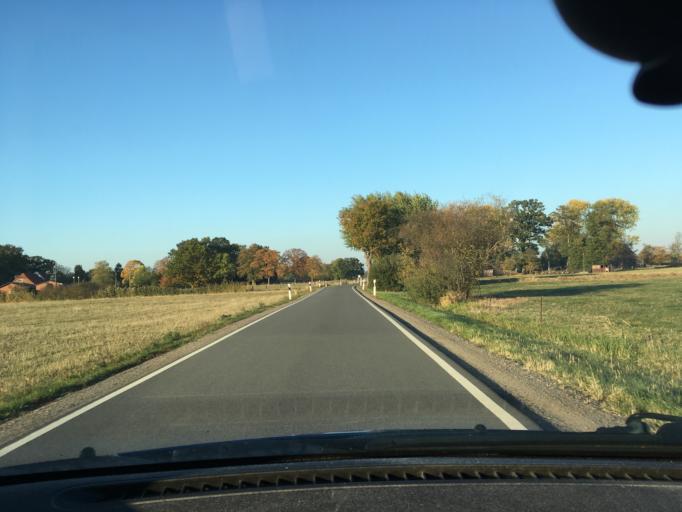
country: DE
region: Lower Saxony
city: Bleckede
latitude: 53.3181
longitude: 10.7933
